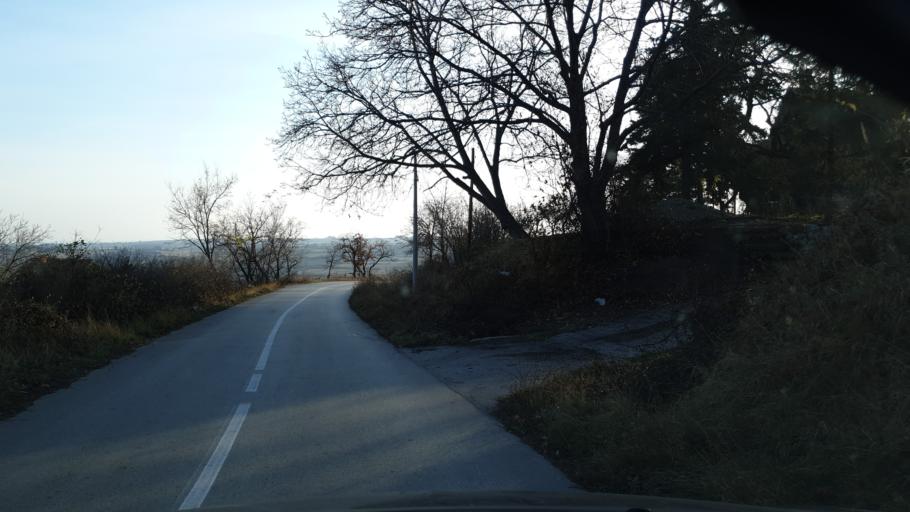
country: RS
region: Central Serbia
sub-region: Borski Okrug
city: Bor
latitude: 44.0482
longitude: 22.0841
